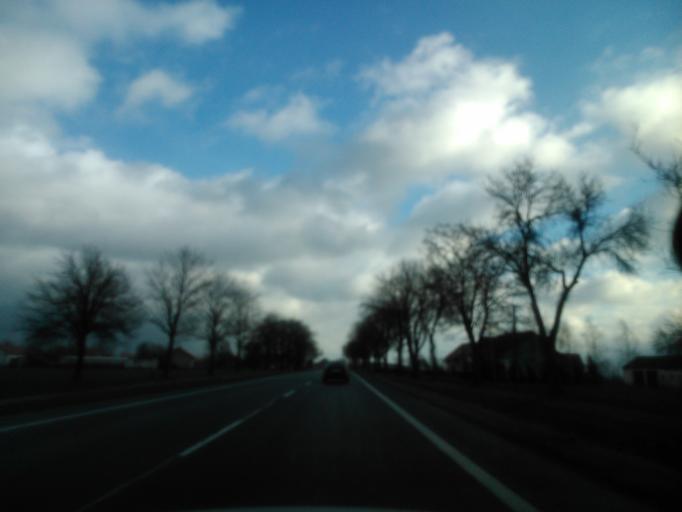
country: PL
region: Masovian Voivodeship
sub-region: Powiat sierpecki
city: Zawidz
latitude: 52.8132
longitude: 19.8041
